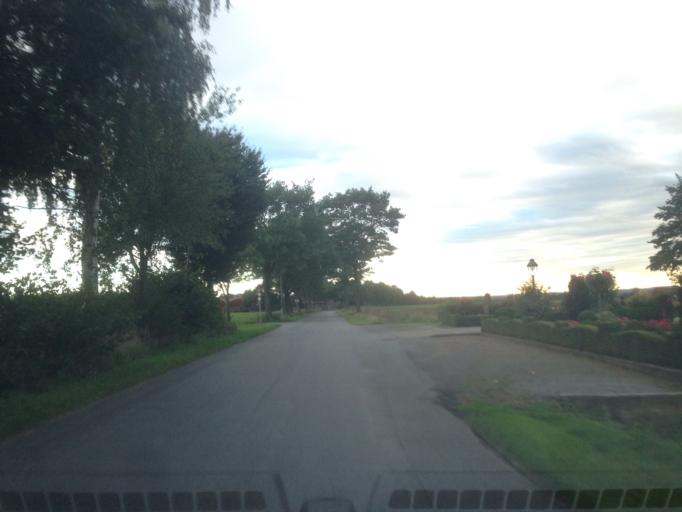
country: DE
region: North Rhine-Westphalia
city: Olfen
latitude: 51.7502
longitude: 7.3909
